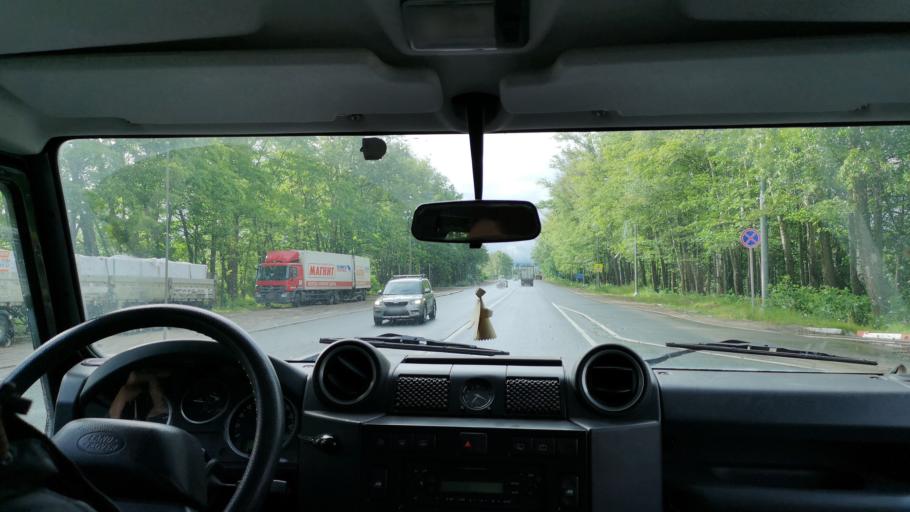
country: RU
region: Moskovskaya
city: Dmitrov
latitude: 56.3618
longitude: 37.4820
